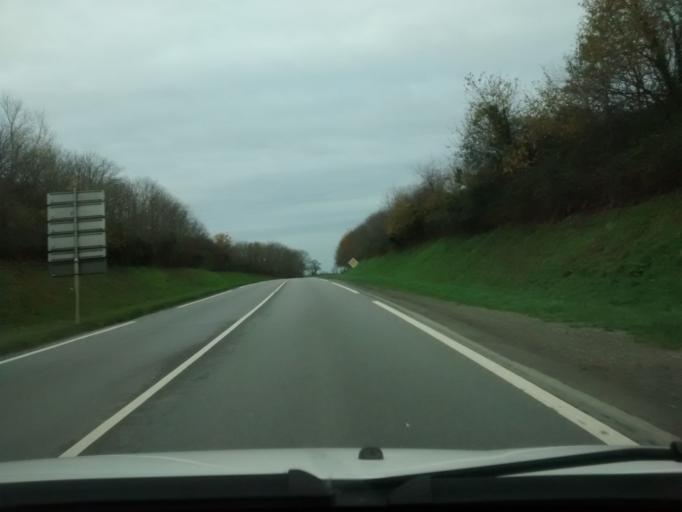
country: FR
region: Brittany
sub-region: Departement d'Ille-et-Vilaine
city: Poce-les-Bois
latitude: 48.1261
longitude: -1.2324
